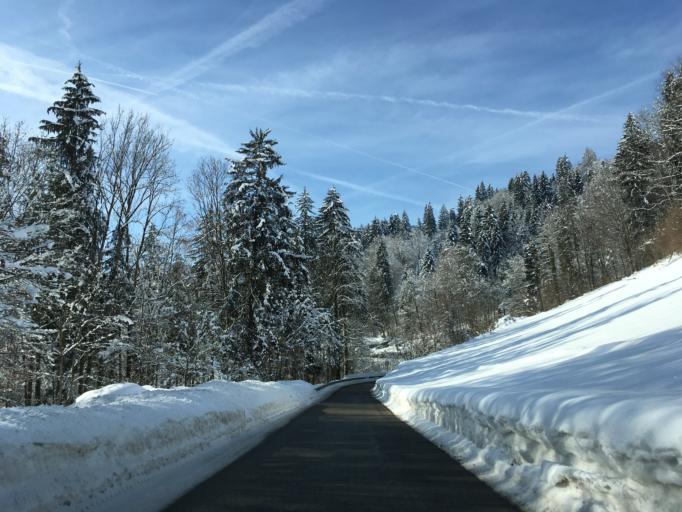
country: DE
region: Bavaria
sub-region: Upper Bavaria
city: Oberaudorf
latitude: 47.6609
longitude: 12.1368
